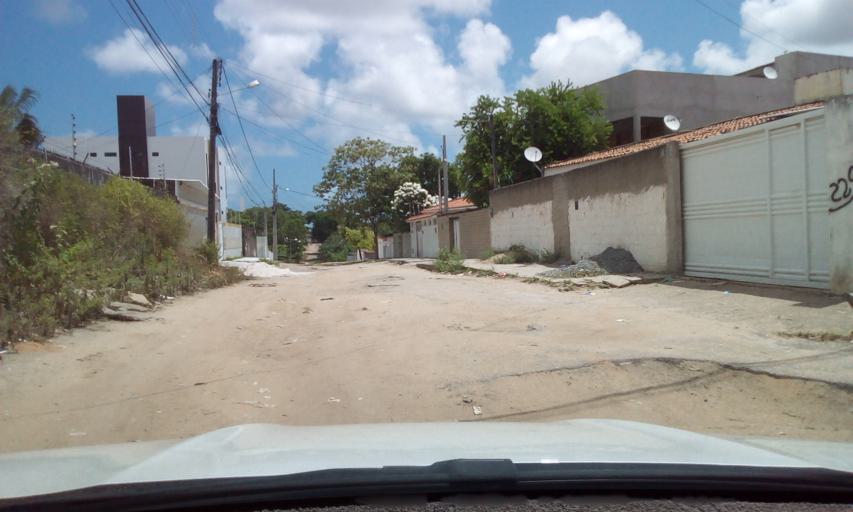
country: BR
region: Paraiba
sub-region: Joao Pessoa
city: Joao Pessoa
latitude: -7.1820
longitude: -34.8639
